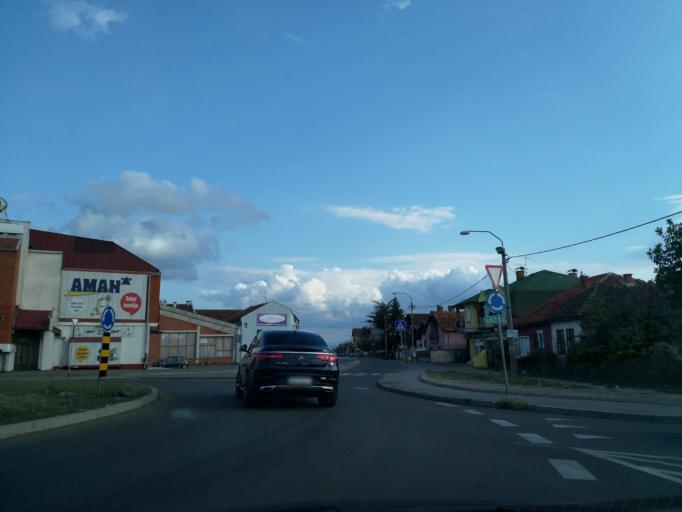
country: RS
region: Central Serbia
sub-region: Pomoravski Okrug
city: Paracin
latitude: 43.8533
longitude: 21.4130
